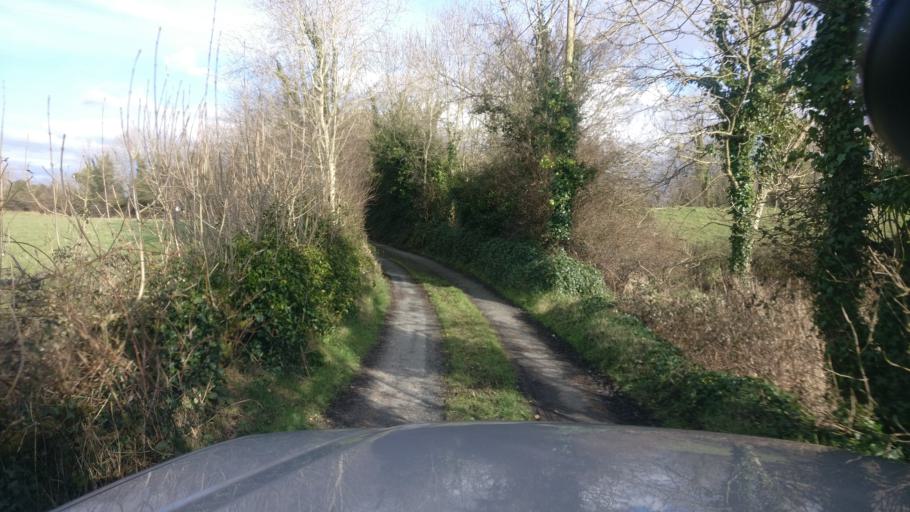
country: IE
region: Connaught
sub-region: County Galway
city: Loughrea
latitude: 53.1820
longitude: -8.4239
